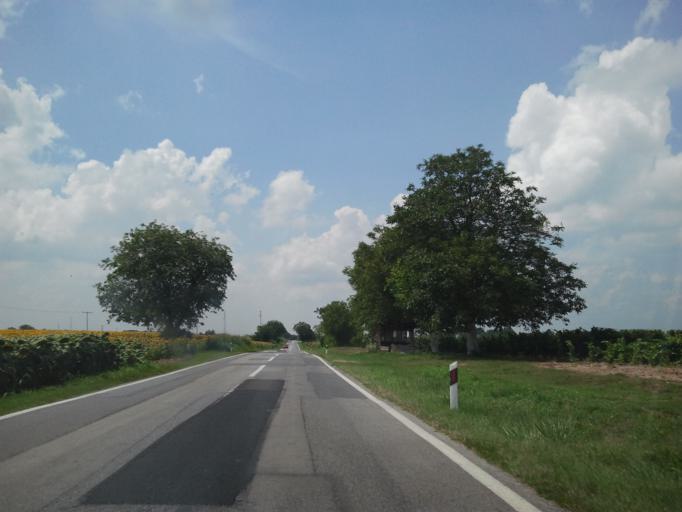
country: HR
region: Vukovarsko-Srijemska
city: Lovas
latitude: 45.2562
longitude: 19.1868
